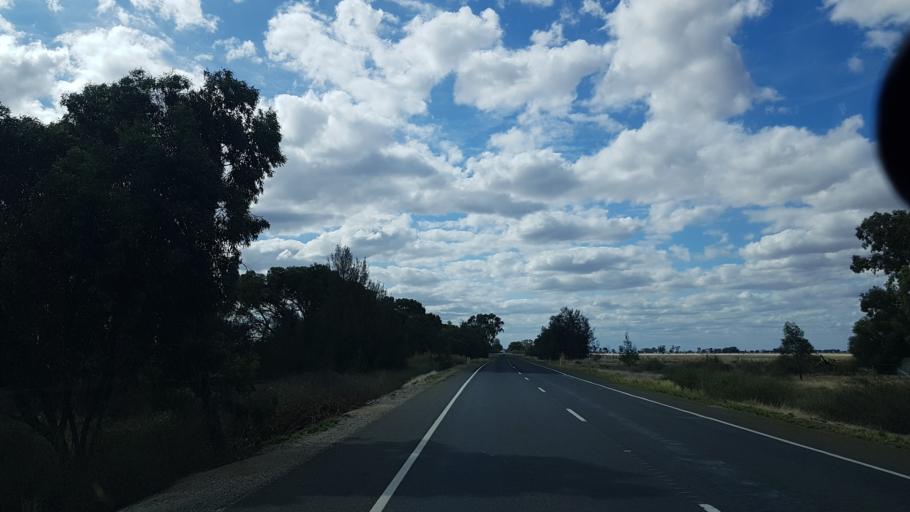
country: AU
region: Victoria
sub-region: Swan Hill
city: Swan Hill
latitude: -35.9879
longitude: 143.9459
